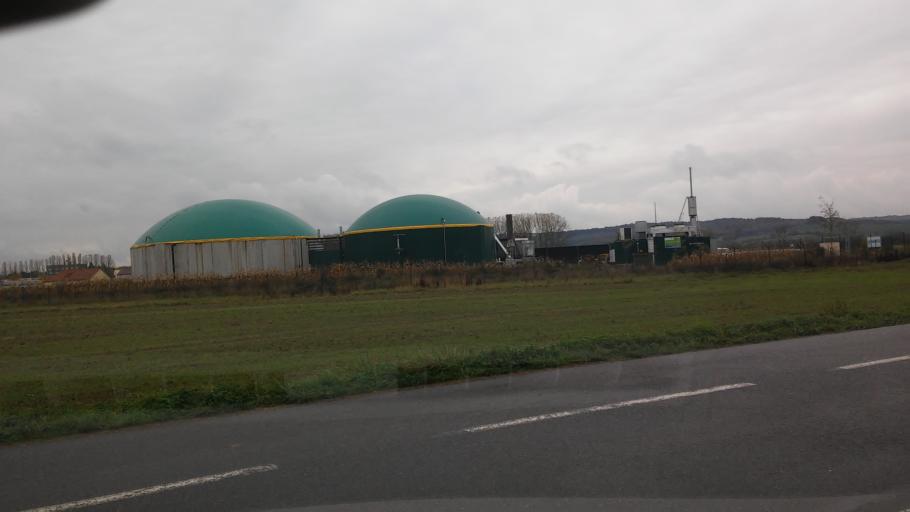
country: FR
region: Lorraine
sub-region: Departement de la Moselle
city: Boulay-Moselle
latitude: 49.1812
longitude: 6.4777
